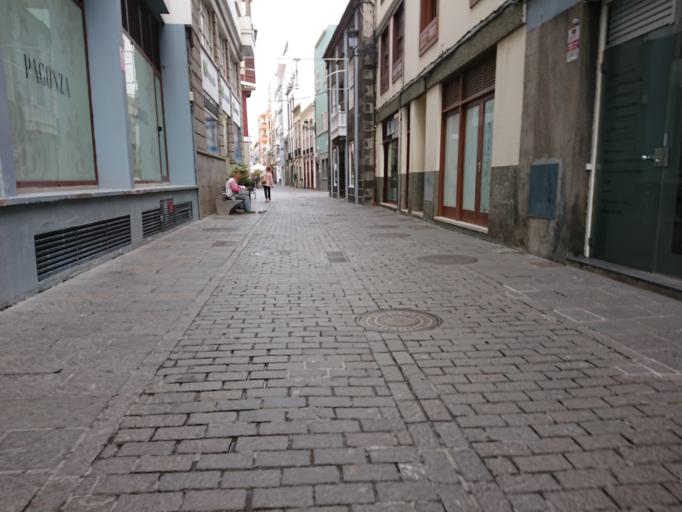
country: ES
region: Canary Islands
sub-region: Provincia de Santa Cruz de Tenerife
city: Santa Cruz de la Palma
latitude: 28.6821
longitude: -17.7654
